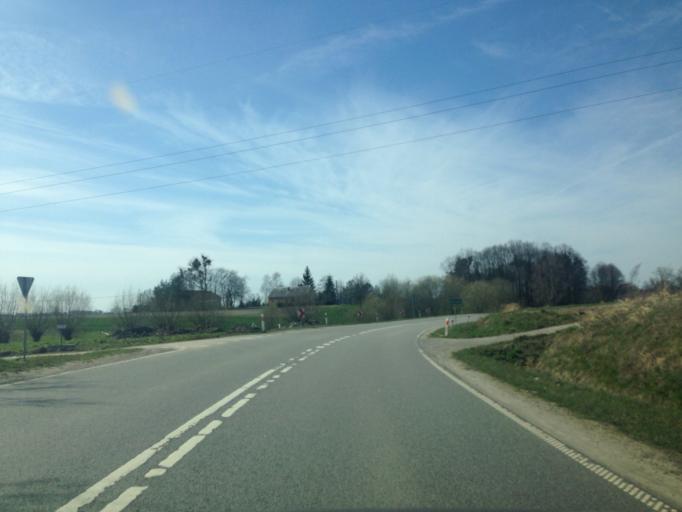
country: PL
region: Pomeranian Voivodeship
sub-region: Powiat starogardzki
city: Smetowo Graniczne
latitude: 53.7393
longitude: 18.7009
